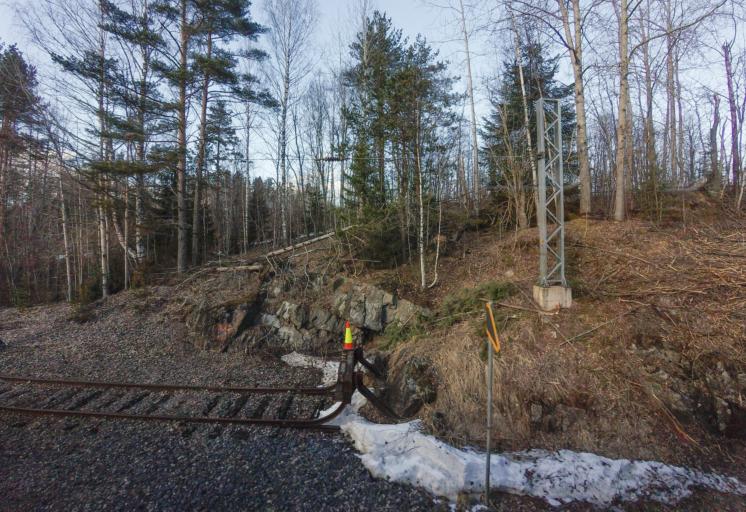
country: FI
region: South Karelia
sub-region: Imatra
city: Simpele
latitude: 61.4249
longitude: 29.3855
